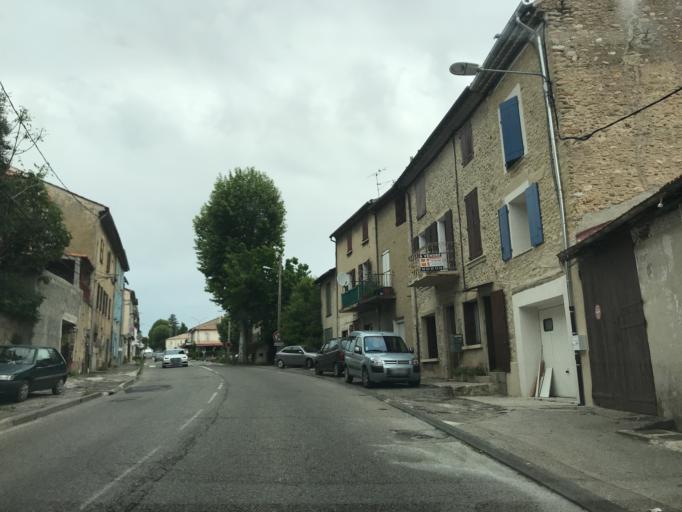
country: FR
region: Provence-Alpes-Cote d'Azur
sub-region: Departement des Alpes-de-Haute-Provence
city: Oraison
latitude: 43.9256
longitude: 5.8907
